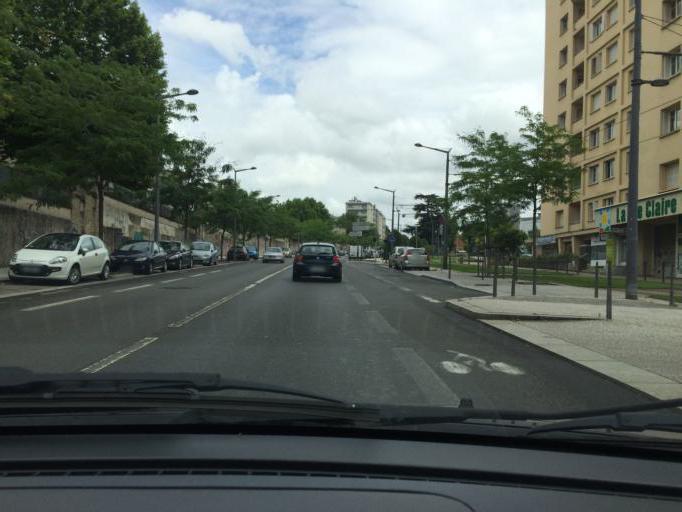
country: FR
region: Rhone-Alpes
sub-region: Departement du Rhone
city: Villeurbanne
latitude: 45.7422
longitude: 4.8821
